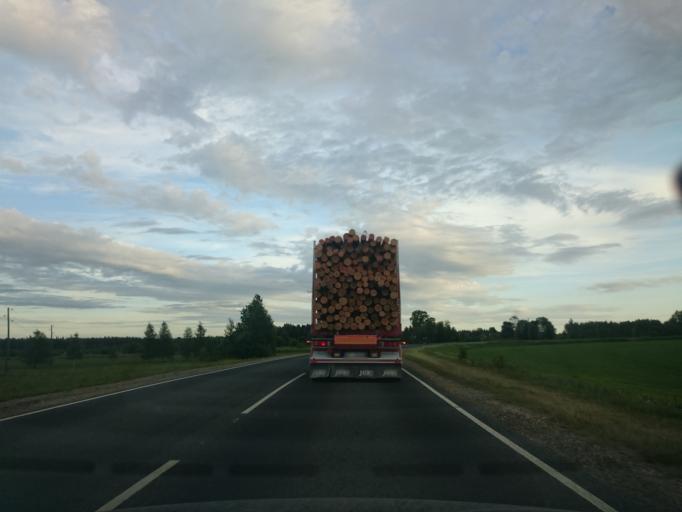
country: LV
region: Incukalns
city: Incukalns
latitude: 57.0968
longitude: 24.7016
